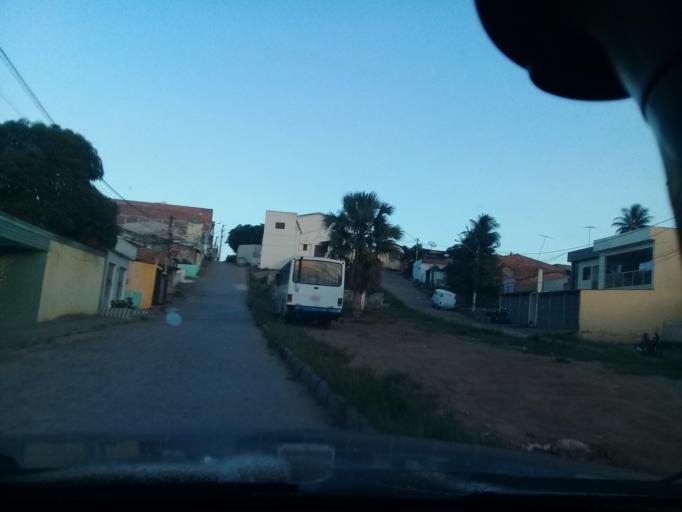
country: BR
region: Pernambuco
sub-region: Vitoria De Santo Antao
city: Vitoria de Santo Antao
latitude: -8.1289
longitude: -35.2952
